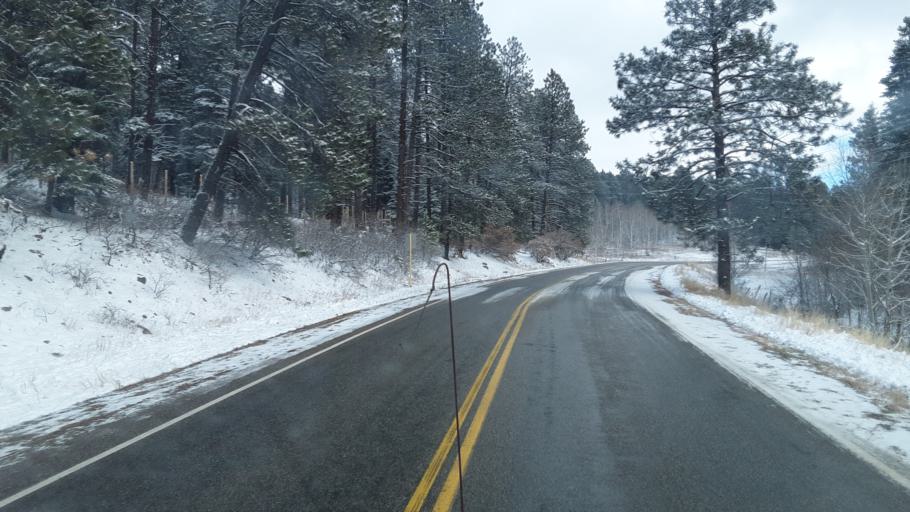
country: US
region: Colorado
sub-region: La Plata County
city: Bayfield
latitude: 37.3578
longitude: -107.6658
